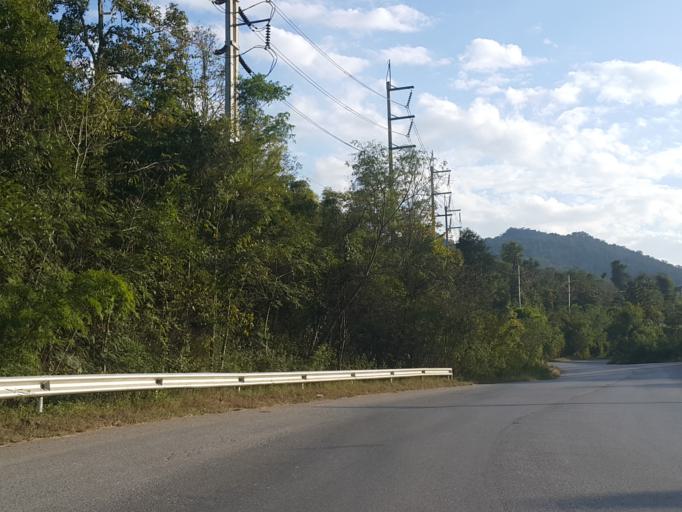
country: TH
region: Lampang
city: Chae Hom
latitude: 18.5228
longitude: 99.5573
